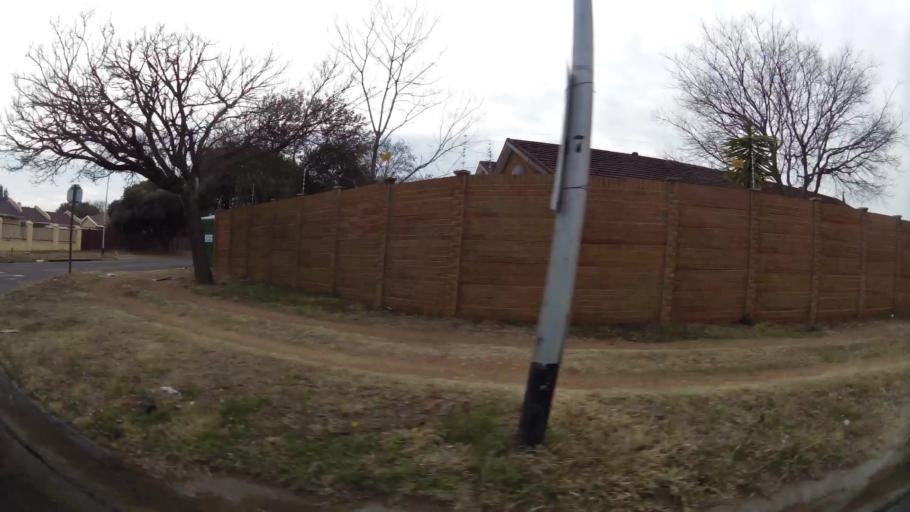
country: ZA
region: Orange Free State
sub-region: Mangaung Metropolitan Municipality
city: Bloemfontein
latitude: -29.1150
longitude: 26.1655
